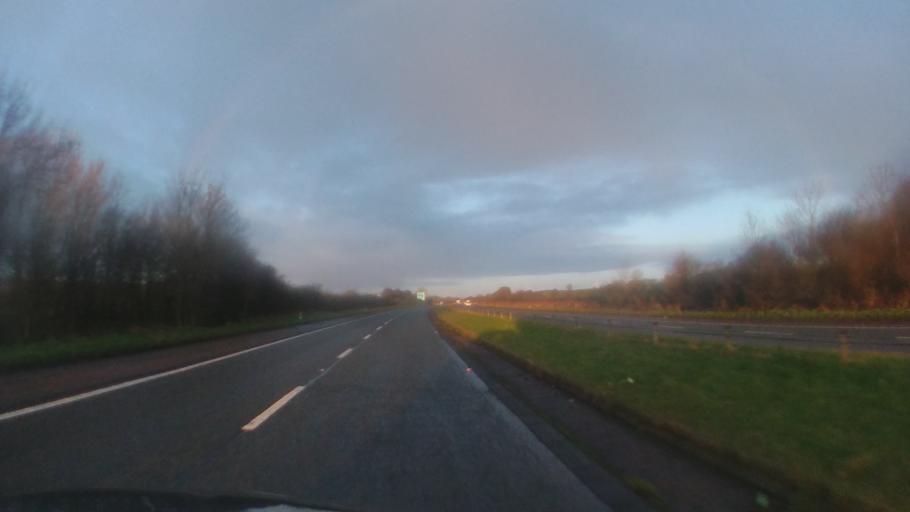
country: GB
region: Northern Ireland
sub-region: Antrim Borough
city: Antrim
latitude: 54.7310
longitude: -6.1756
